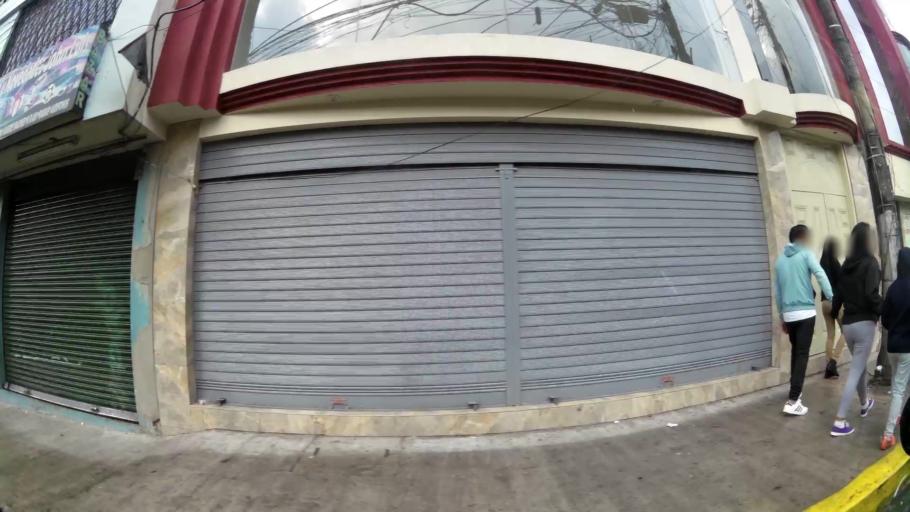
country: EC
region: Pichincha
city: Quito
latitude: -0.1142
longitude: -78.4950
